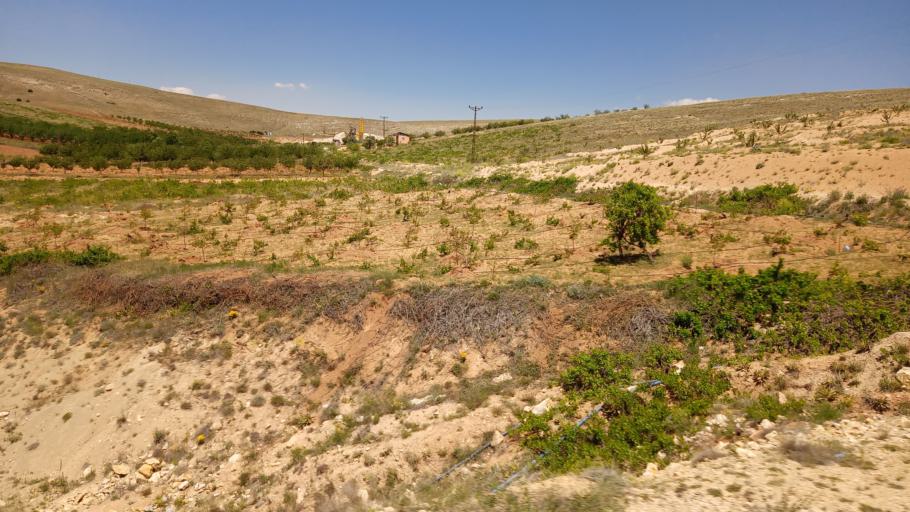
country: TR
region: Malatya
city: Darende
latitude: 38.6012
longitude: 37.4658
